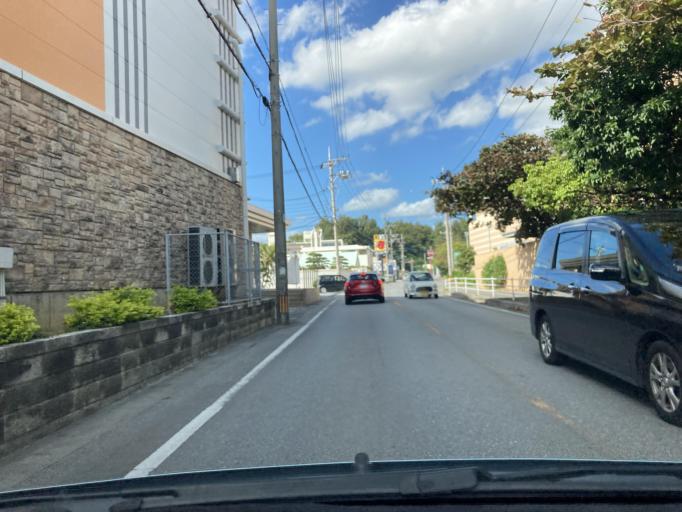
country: JP
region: Okinawa
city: Katsuren-haebaru
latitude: 26.3369
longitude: 127.8438
